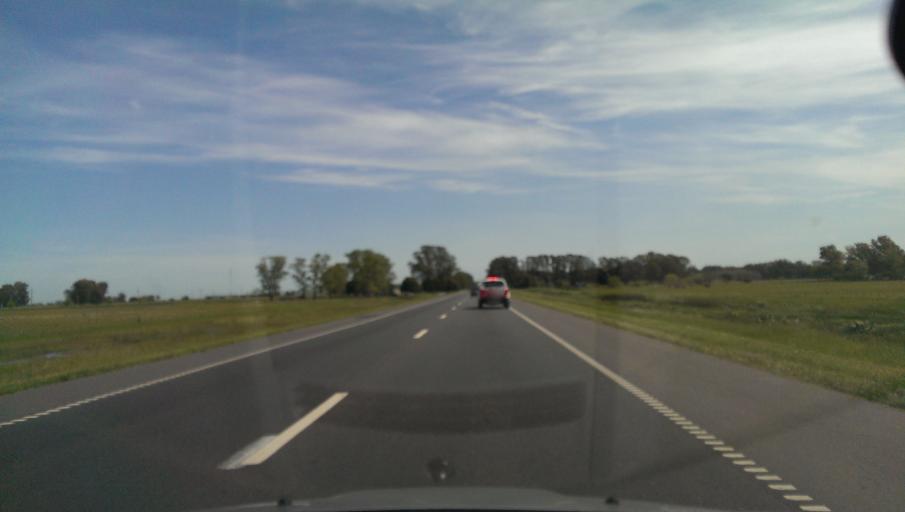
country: AR
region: Buenos Aires
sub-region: Partido de Las Flores
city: Las Flores
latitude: -36.3747
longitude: -59.4750
